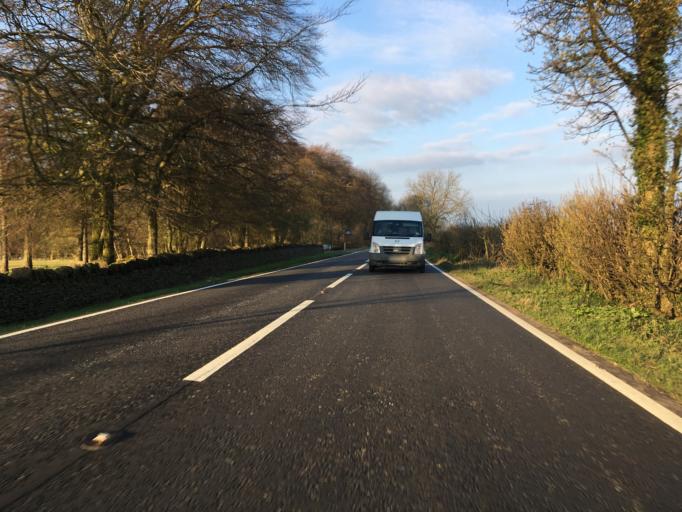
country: GB
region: England
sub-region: Gloucestershire
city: Charlton Kings
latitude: 51.8617
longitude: -2.0299
